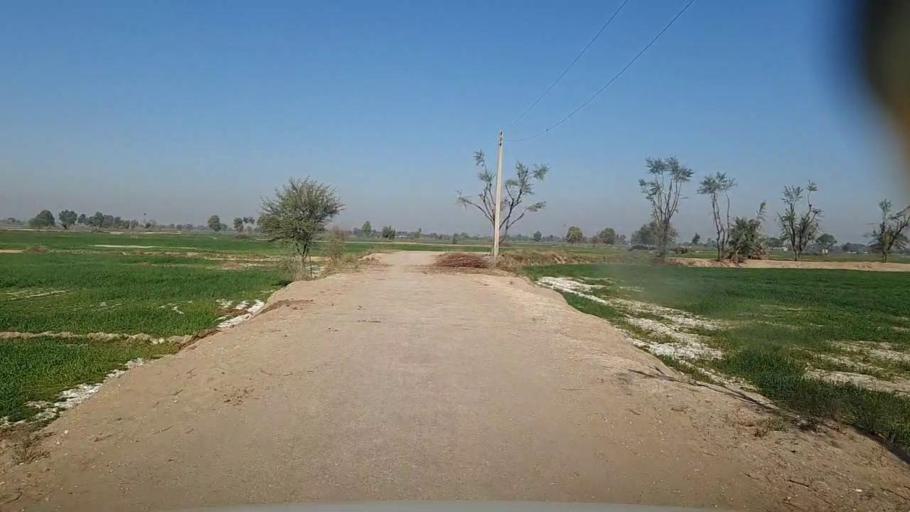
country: PK
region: Sindh
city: Khairpur
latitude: 28.0610
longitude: 69.7389
